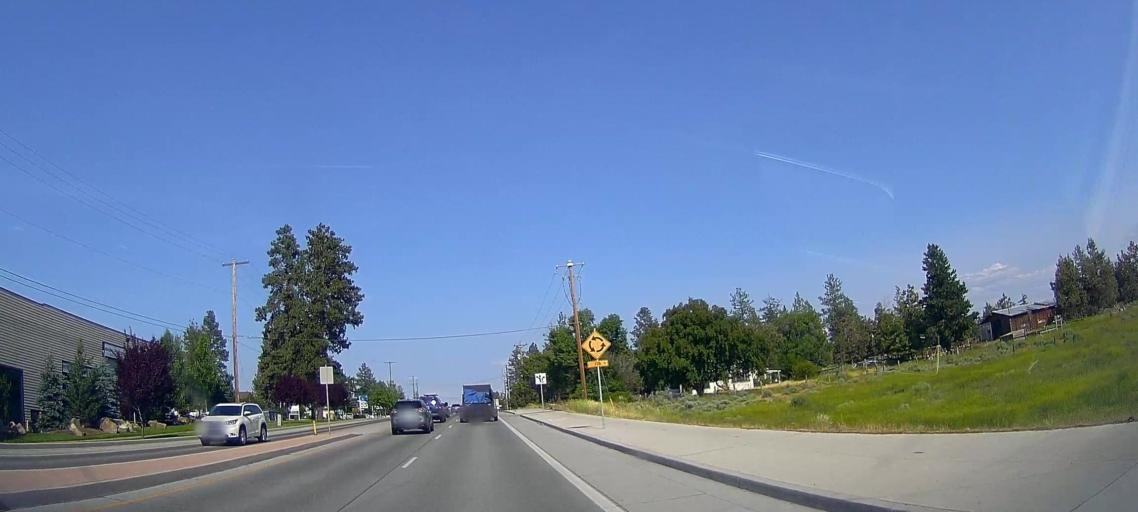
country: US
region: Oregon
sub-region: Deschutes County
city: Bend
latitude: 44.0369
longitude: -121.2873
